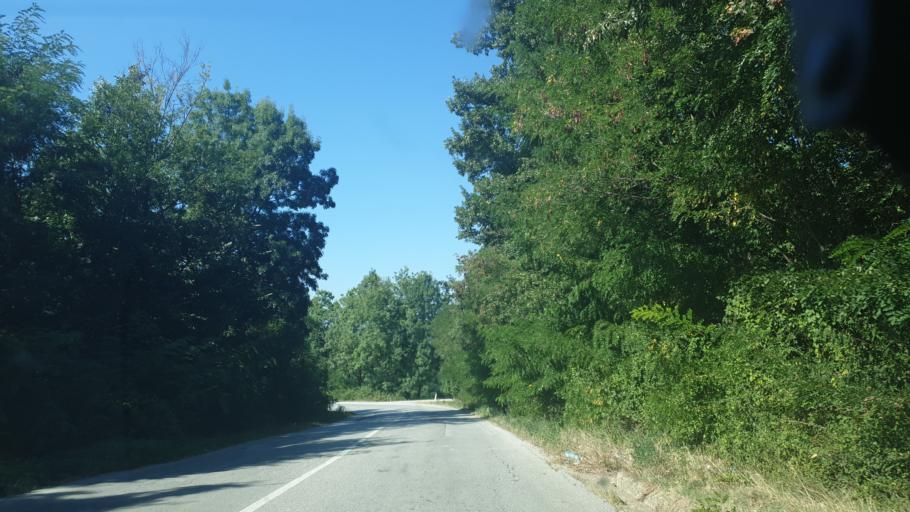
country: RS
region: Central Serbia
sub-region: Kolubarski Okrug
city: Mionica
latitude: 44.2625
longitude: 20.1012
